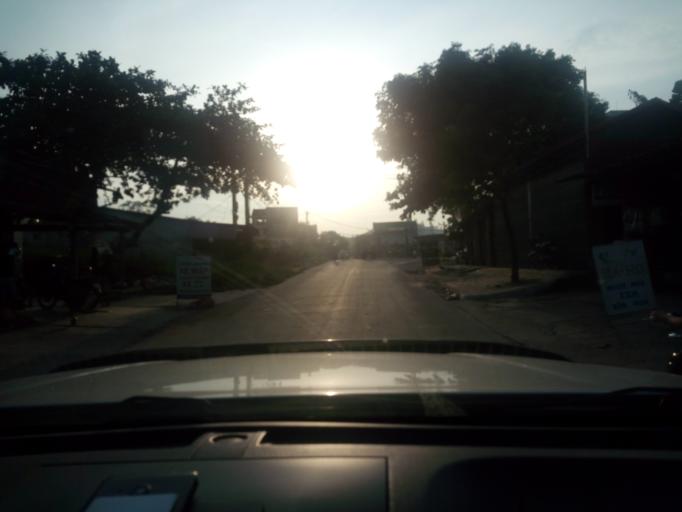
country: VN
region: Yen Bai
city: Co Phuc
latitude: 21.8797
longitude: 104.6752
